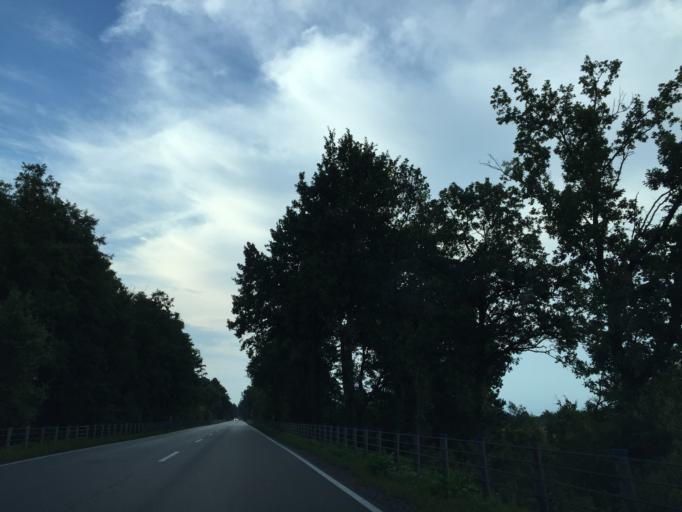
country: PL
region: Masovian Voivodeship
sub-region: Powiat wegrowski
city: Sadowne
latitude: 52.6503
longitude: 21.8466
